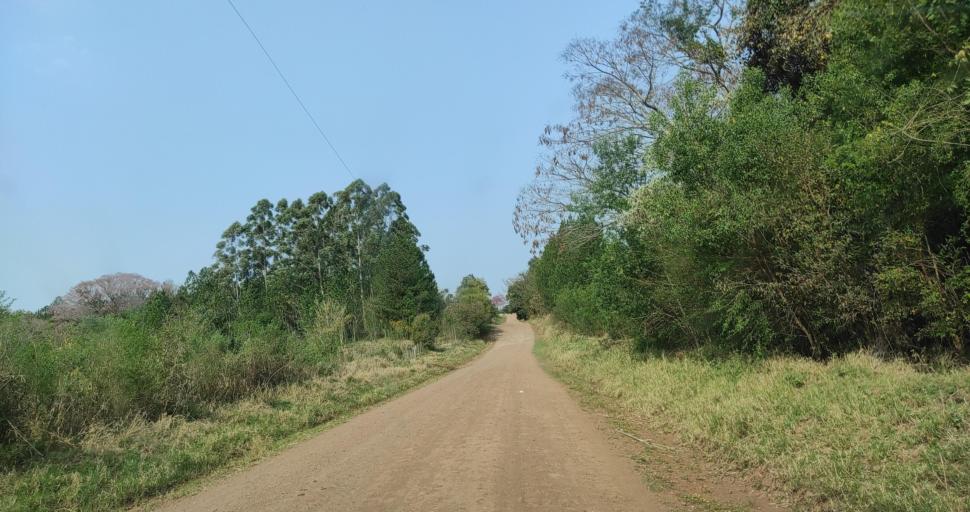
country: AR
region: Misiones
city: Cerro Azul
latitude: -27.6261
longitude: -55.5259
